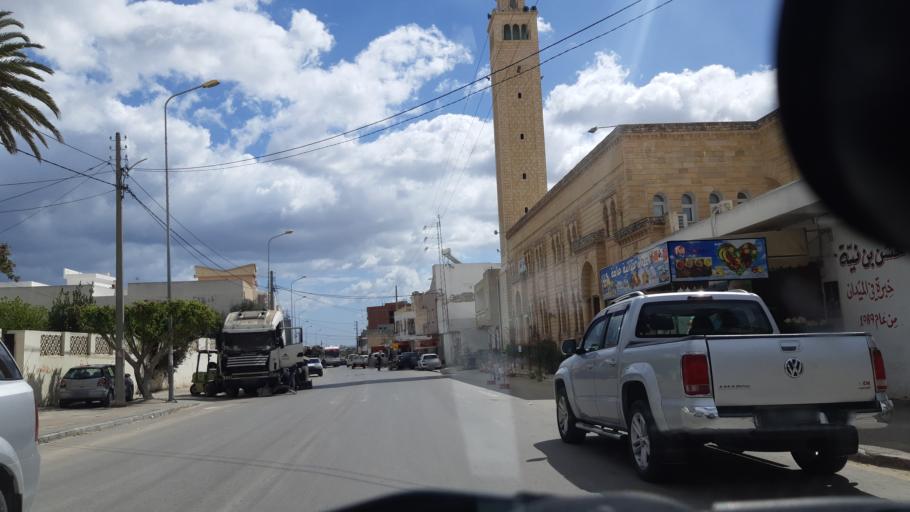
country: TN
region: Susah
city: Akouda
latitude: 35.8737
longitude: 10.5455
